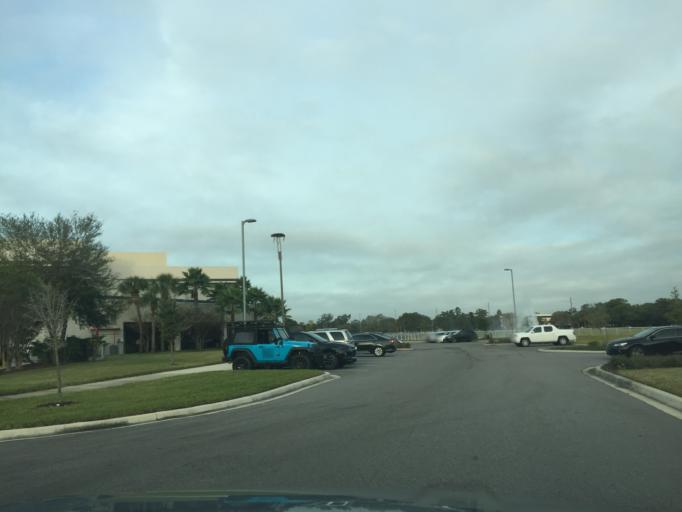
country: US
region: Florida
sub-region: Hillsborough County
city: Town 'n' Country
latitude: 27.9798
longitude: -82.5520
